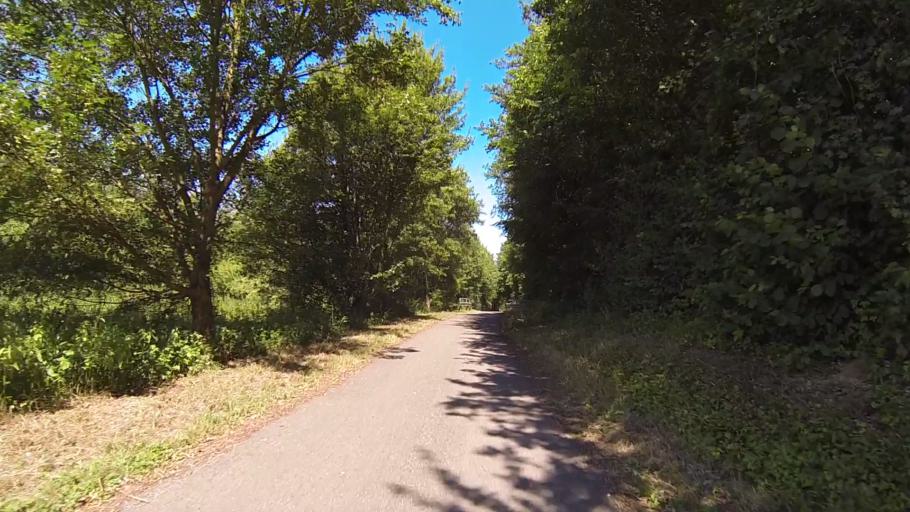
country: LU
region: Grevenmacher
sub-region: Canton de Grevenmacher
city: Grevenmacher
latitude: 49.6802
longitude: 6.4503
